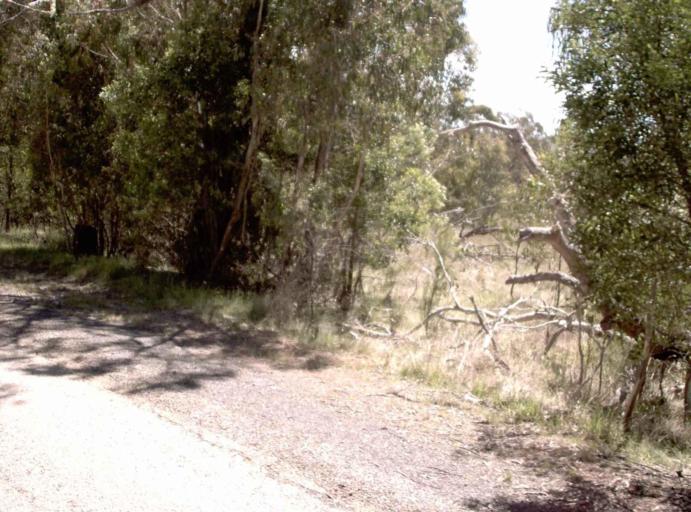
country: AU
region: Victoria
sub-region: East Gippsland
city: Lakes Entrance
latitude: -37.1299
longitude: 148.2449
